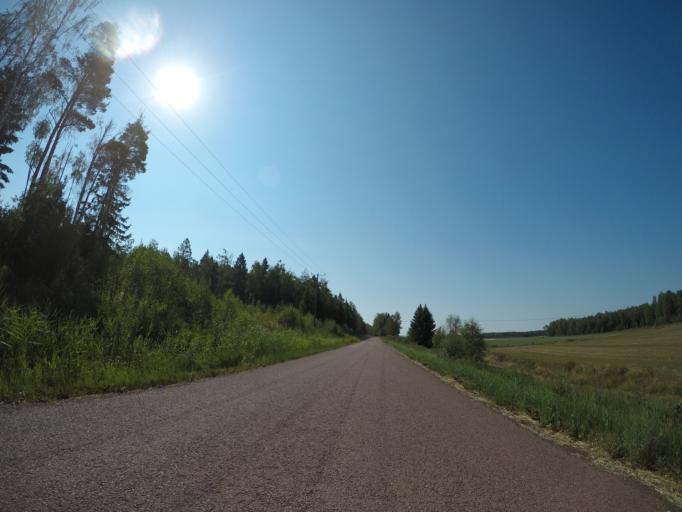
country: AX
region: Alands landsbygd
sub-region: Saltvik
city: Saltvik
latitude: 60.2262
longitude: 20.0102
